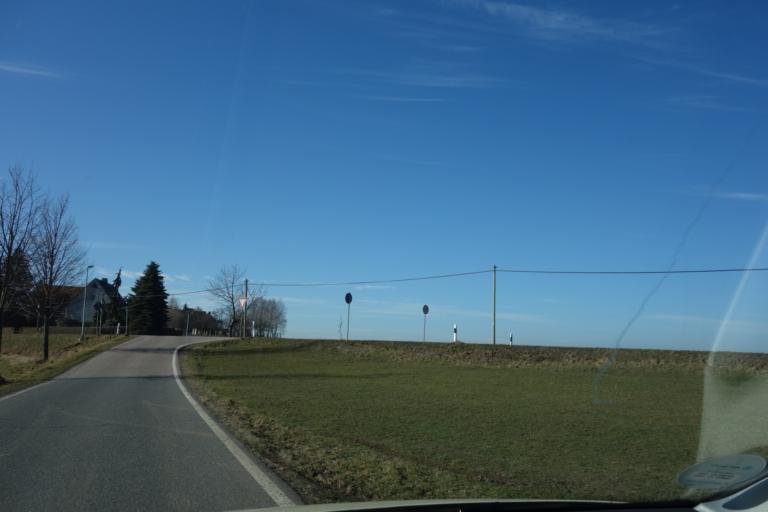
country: DE
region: Saxony
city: Hainichen
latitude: 50.9665
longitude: 13.1826
